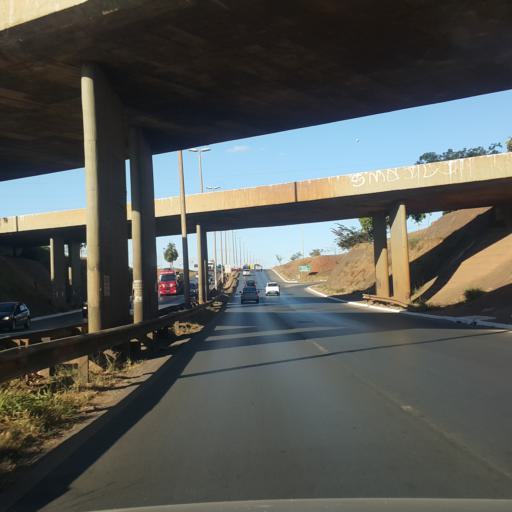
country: BR
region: Federal District
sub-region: Brasilia
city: Brasilia
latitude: -15.7924
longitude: -48.0539
